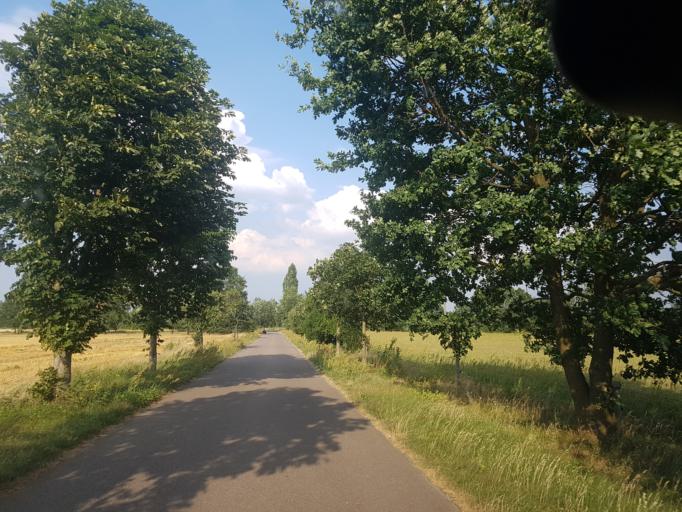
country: DE
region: Brandenburg
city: Herzberg
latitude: 51.6871
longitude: 13.2811
